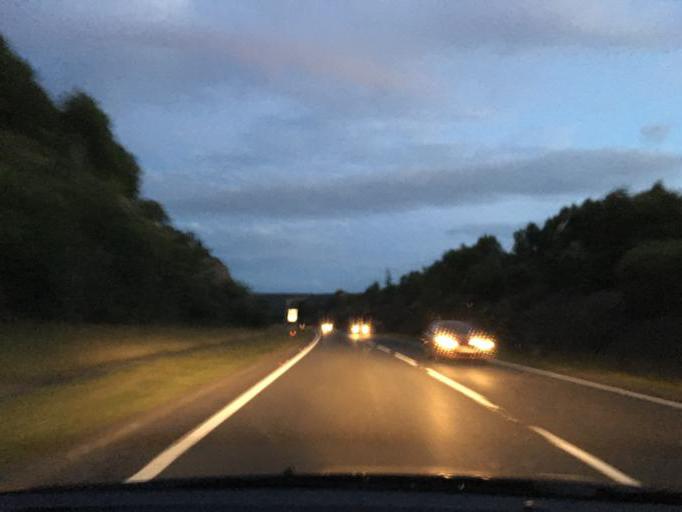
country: GB
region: Scotland
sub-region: Perth and Kinross
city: Aberfeldy
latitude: 56.7900
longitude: -4.0116
